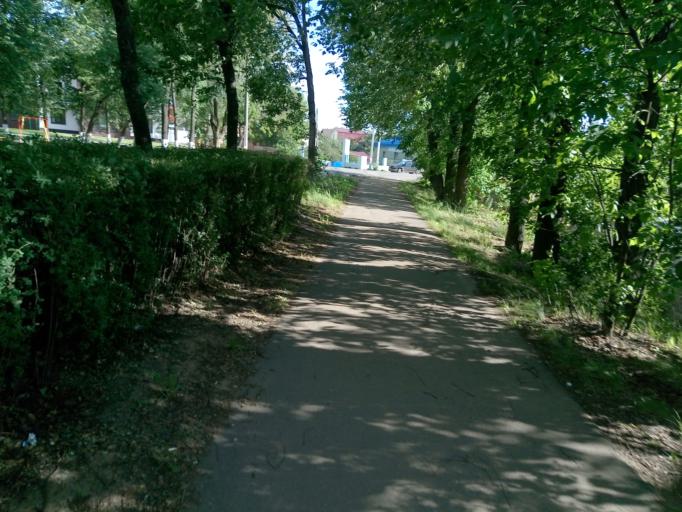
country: RU
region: Jaroslavl
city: Yaroslavl
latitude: 57.6389
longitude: 39.9118
